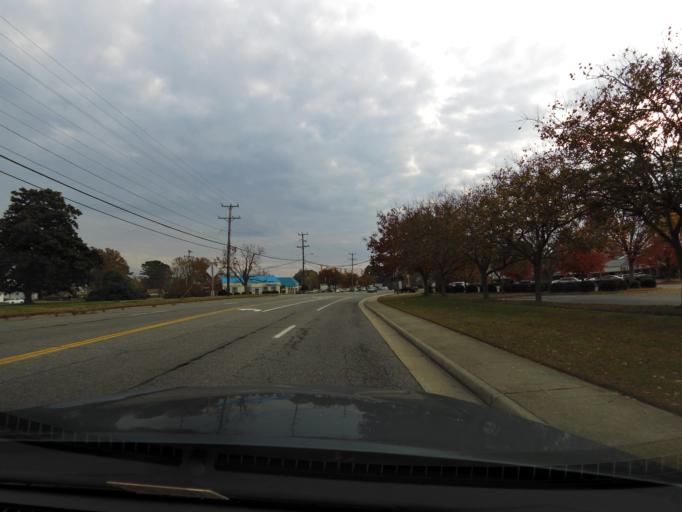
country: US
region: Virginia
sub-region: City of Hampton
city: Hampton
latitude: 37.0116
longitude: -76.3531
